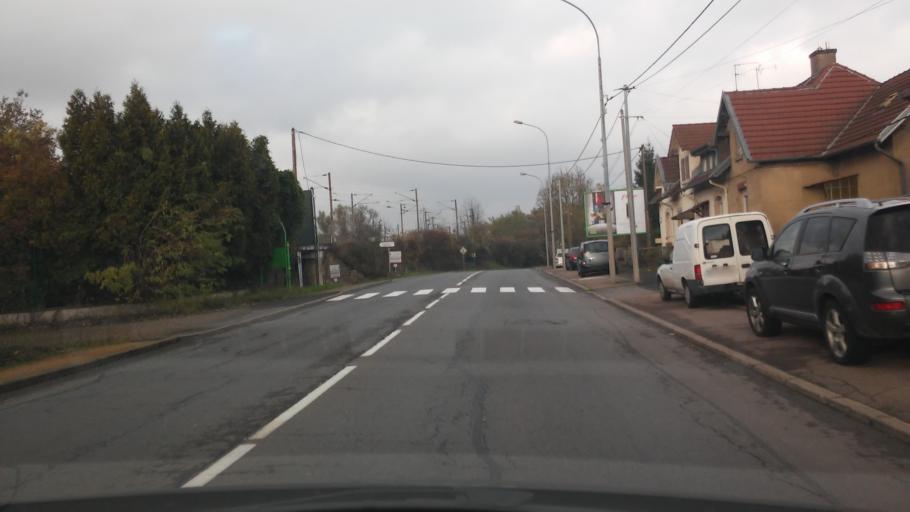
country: FR
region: Lorraine
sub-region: Departement de la Moselle
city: Terville
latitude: 49.3299
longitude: 6.1527
